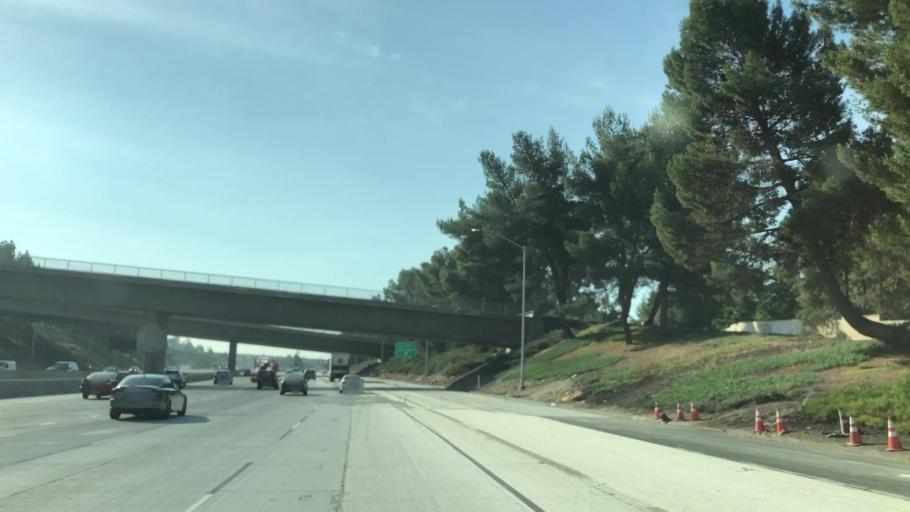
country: US
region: California
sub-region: Los Angeles County
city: La Crescenta-Montrose
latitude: 34.2126
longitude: -118.2301
